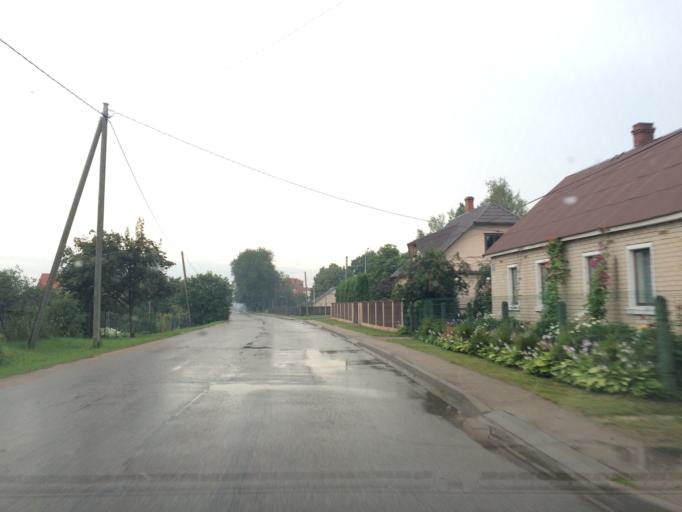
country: LV
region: Rezekne
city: Rezekne
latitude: 56.5212
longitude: 27.3498
